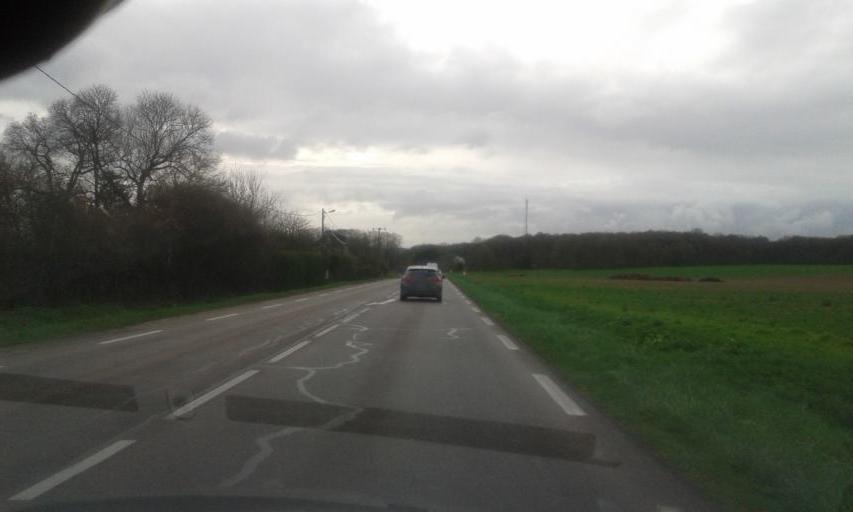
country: FR
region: Haute-Normandie
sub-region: Departement de l'Eure
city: Fleury-sur-Andelle
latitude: 49.3759
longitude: 1.3284
